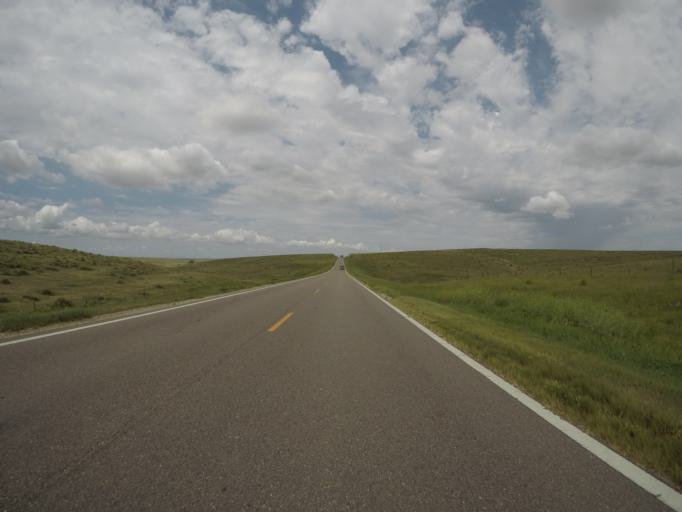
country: US
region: Kansas
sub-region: Rawlins County
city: Atwood
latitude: 39.7390
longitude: -101.0533
